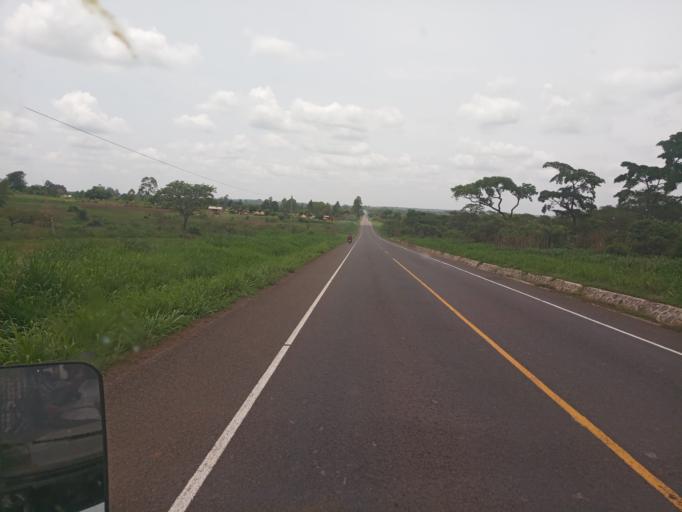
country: UG
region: Northern Region
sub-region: Oyam District
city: Oyam
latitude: 2.1794
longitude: 32.2253
